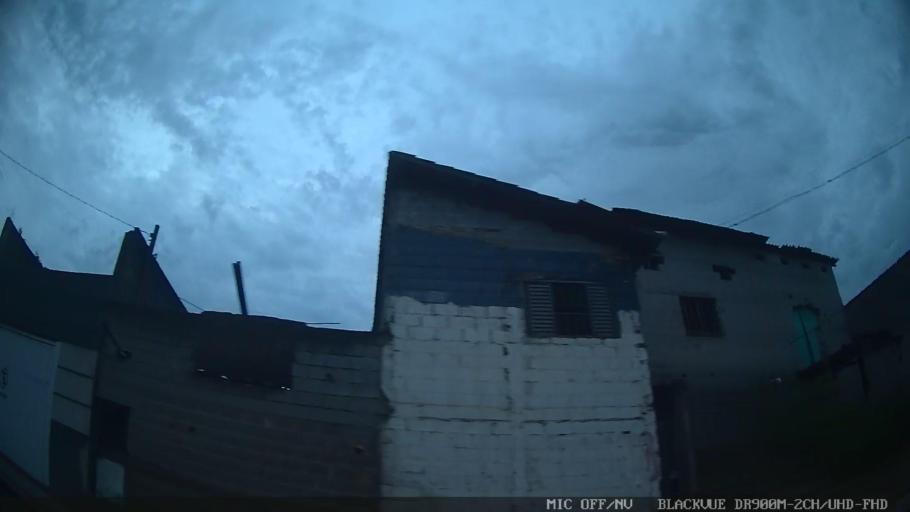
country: BR
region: Sao Paulo
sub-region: Itatiba
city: Itatiba
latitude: -22.8770
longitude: -46.7935
